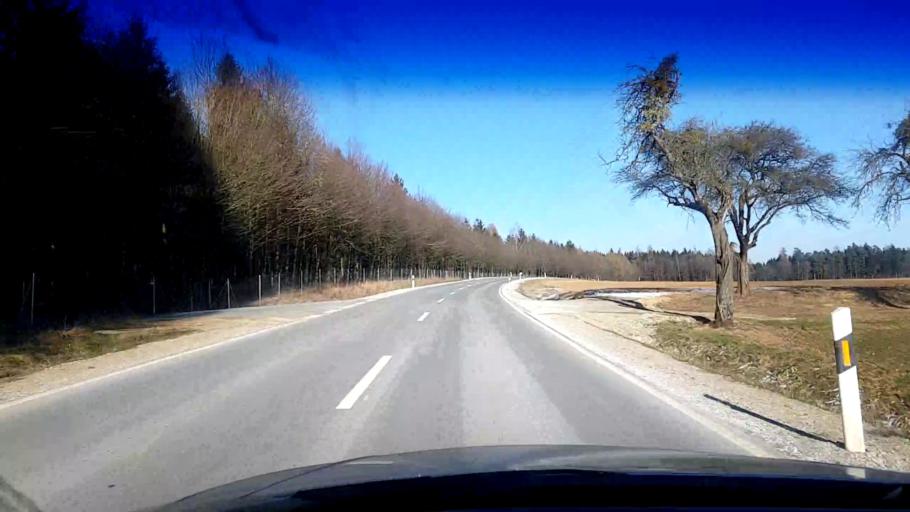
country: DE
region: Bavaria
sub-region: Upper Franconia
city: Heiligenstadt
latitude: 49.8761
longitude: 11.1891
